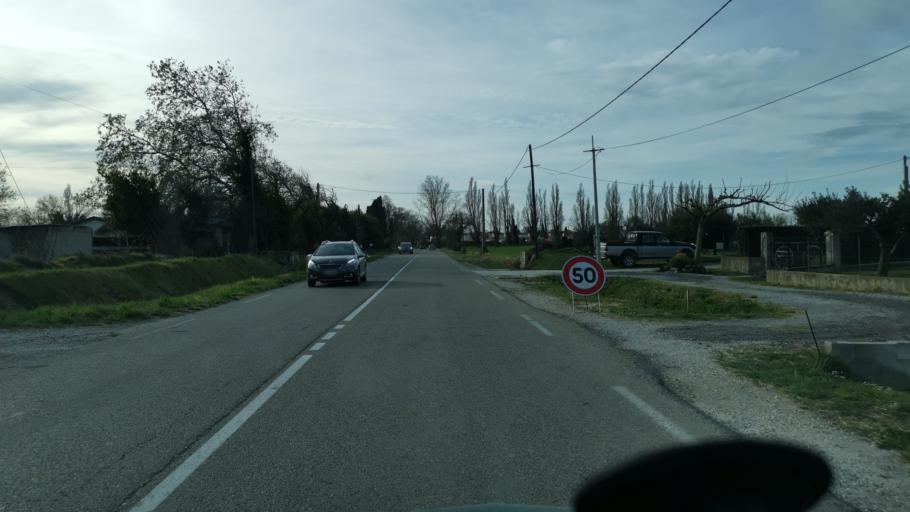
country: FR
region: Provence-Alpes-Cote d'Azur
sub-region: Departement des Bouches-du-Rhone
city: Saint-Martin-de-Crau
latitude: 43.6420
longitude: 4.7340
